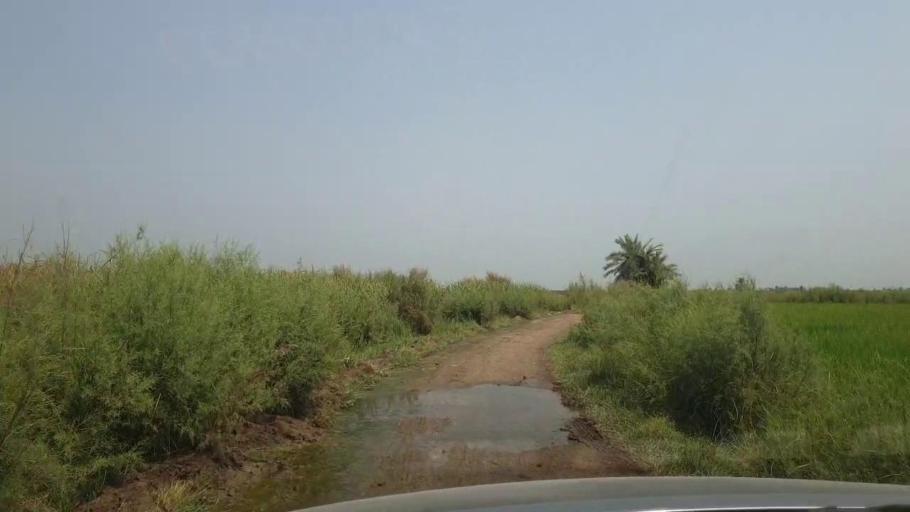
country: PK
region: Sindh
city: Madeji
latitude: 27.8139
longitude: 68.5089
